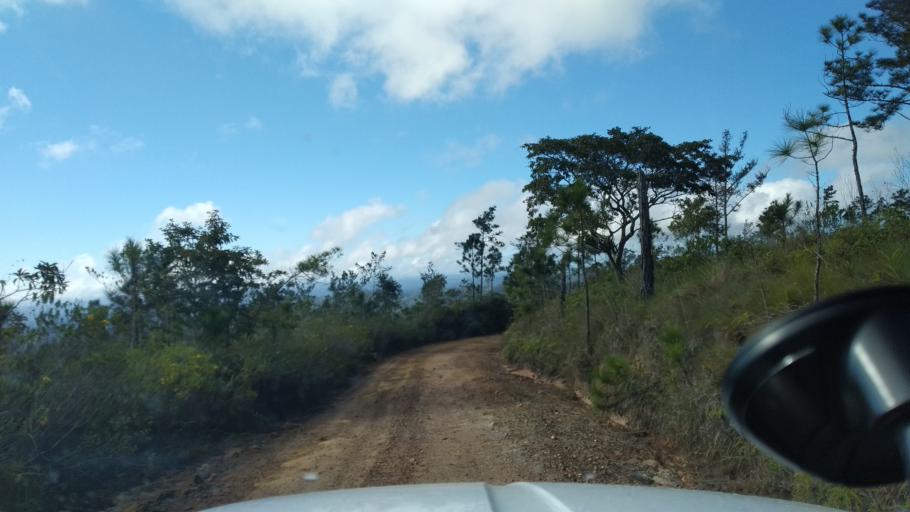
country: BZ
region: Cayo
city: Belmopan
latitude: 16.9972
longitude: -88.8328
